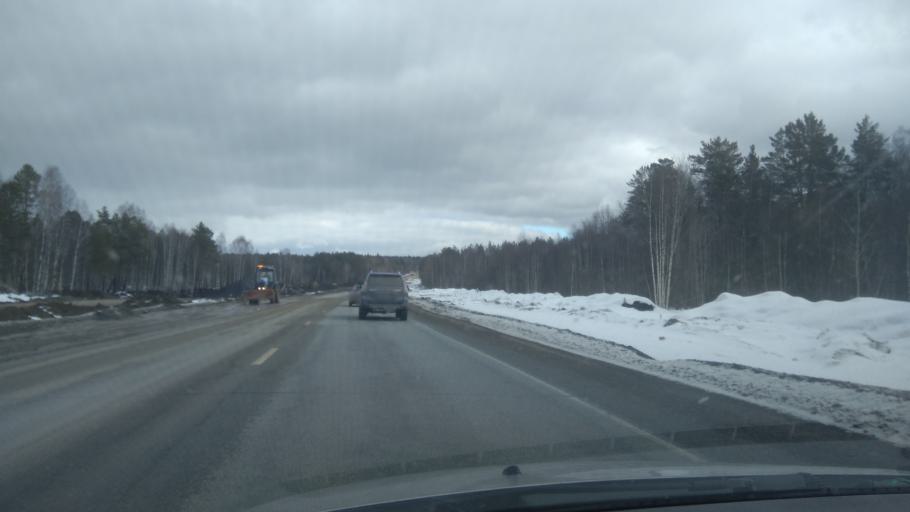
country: RU
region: Sverdlovsk
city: Bisert'
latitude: 56.8351
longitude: 58.9192
